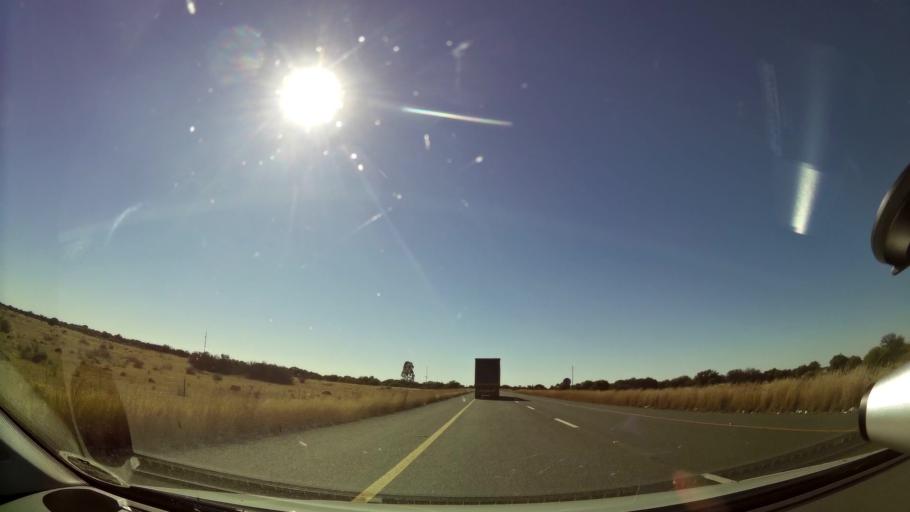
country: ZA
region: Northern Cape
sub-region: Frances Baard District Municipality
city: Warrenton
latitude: -28.0338
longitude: 24.9985
